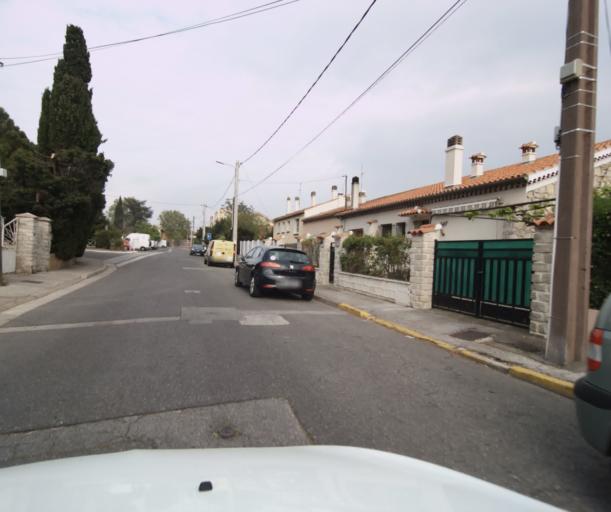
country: FR
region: Provence-Alpes-Cote d'Azur
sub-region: Departement du Var
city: La Valette-du-Var
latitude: 43.1339
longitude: 5.9846
